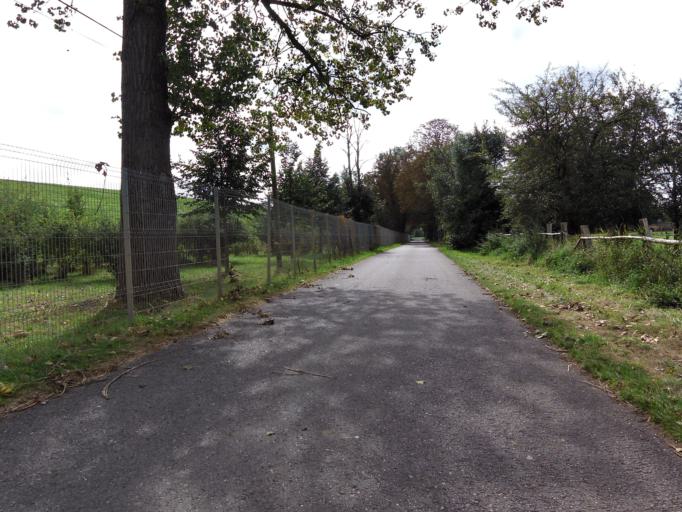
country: DE
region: Saxony-Anhalt
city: Havelberg
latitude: 52.8280
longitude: 12.0570
